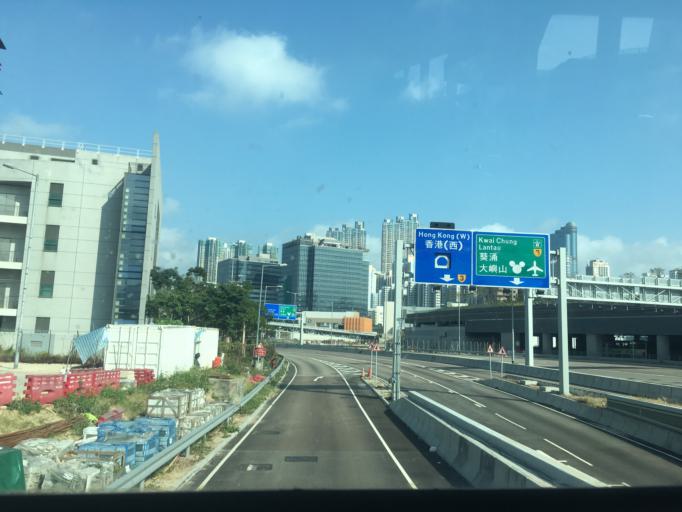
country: HK
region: Kowloon City
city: Kowloon
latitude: 22.3079
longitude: 114.1637
